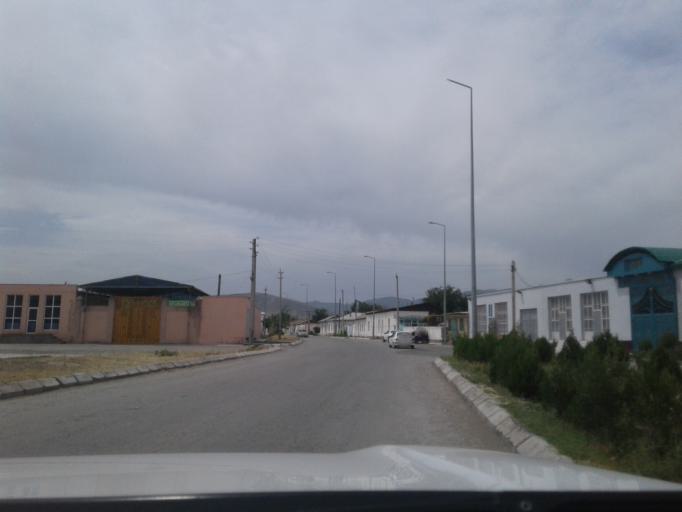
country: TM
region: Balkan
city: Serdar
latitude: 38.9750
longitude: 56.2733
